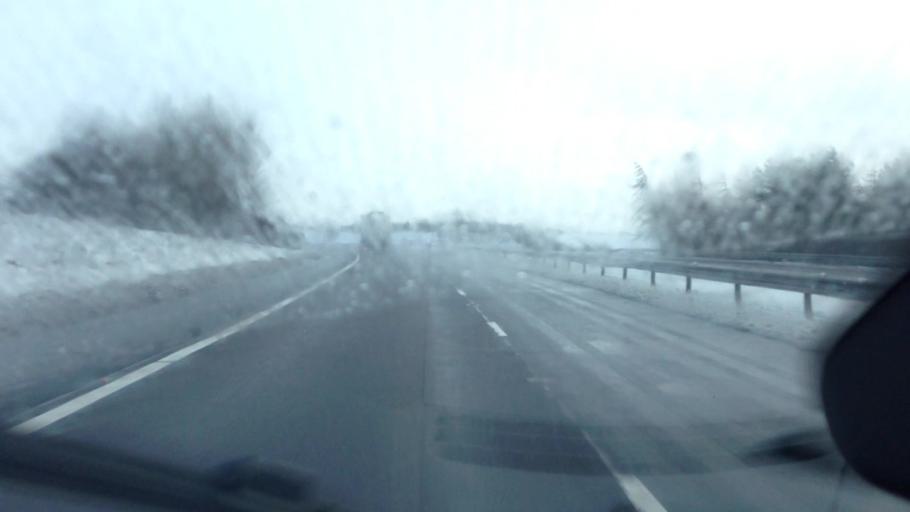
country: GB
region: Scotland
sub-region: South Lanarkshire
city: Blackwood
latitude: 55.6642
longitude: -3.9242
